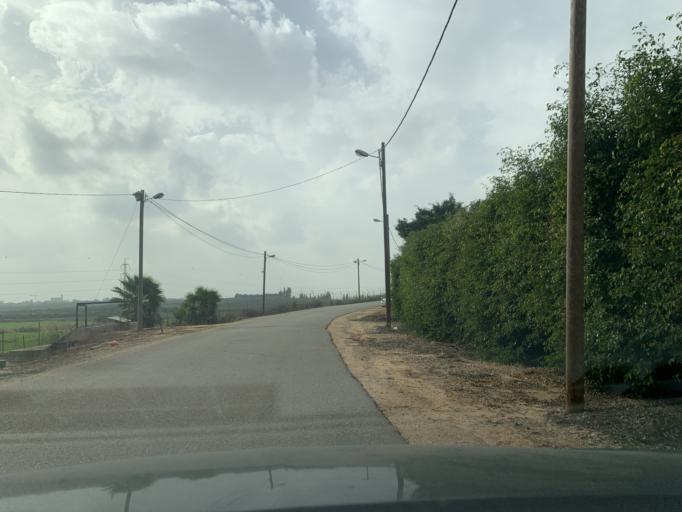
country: IL
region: Central District
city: Tirah
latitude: 32.2145
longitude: 34.9401
